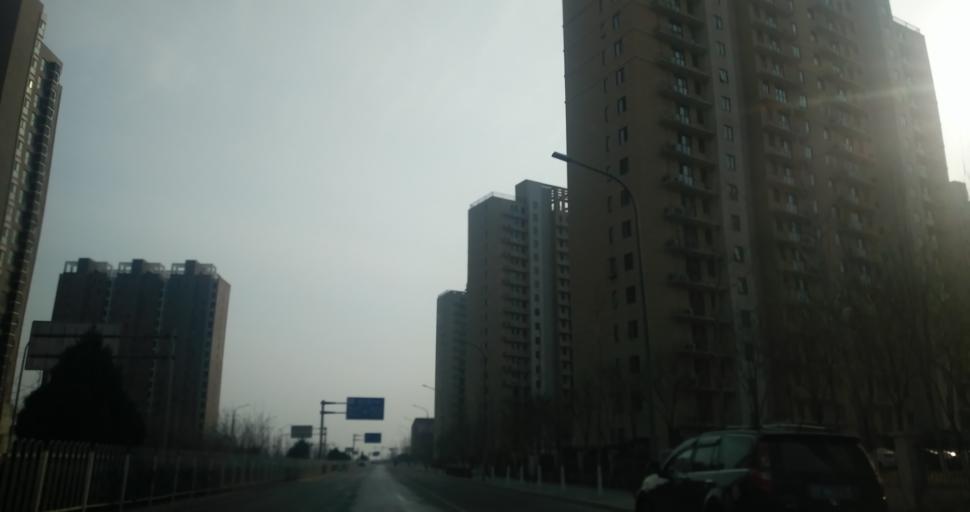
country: CN
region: Beijing
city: Yinghai
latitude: 39.7565
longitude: 116.4910
